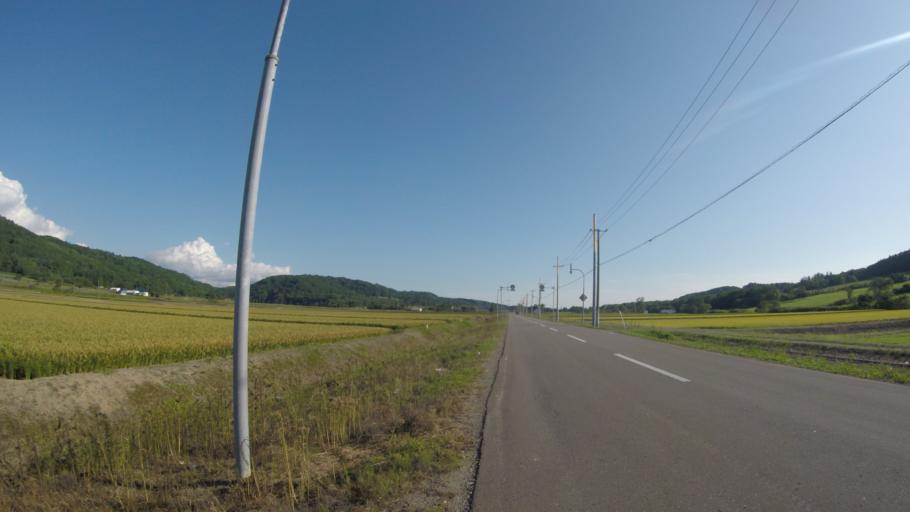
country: JP
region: Hokkaido
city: Iwamizawa
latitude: 43.1980
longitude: 141.8245
